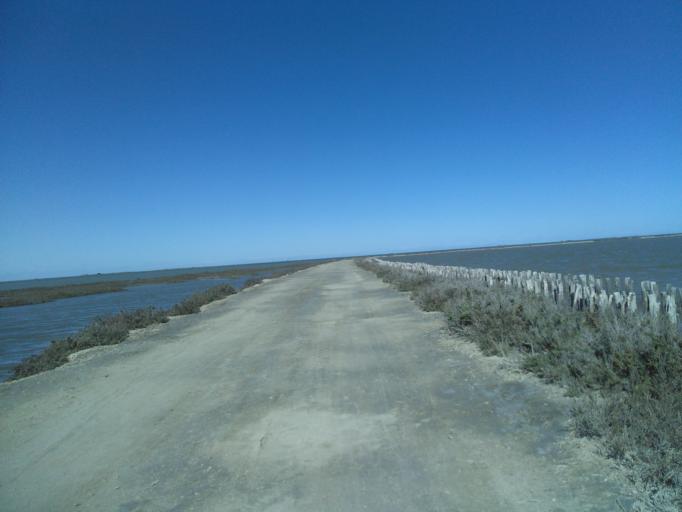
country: FR
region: Provence-Alpes-Cote d'Azur
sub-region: Departement des Bouches-du-Rhone
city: Saintes-Maries-de-la-Mer
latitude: 43.4293
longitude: 4.6188
